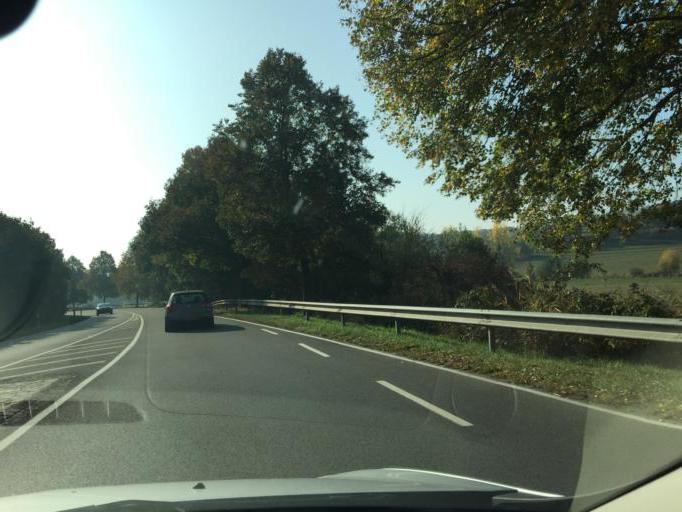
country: LU
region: Grevenmacher
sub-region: Canton de Remich
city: Waldbredimus
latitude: 49.5583
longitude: 6.3055
